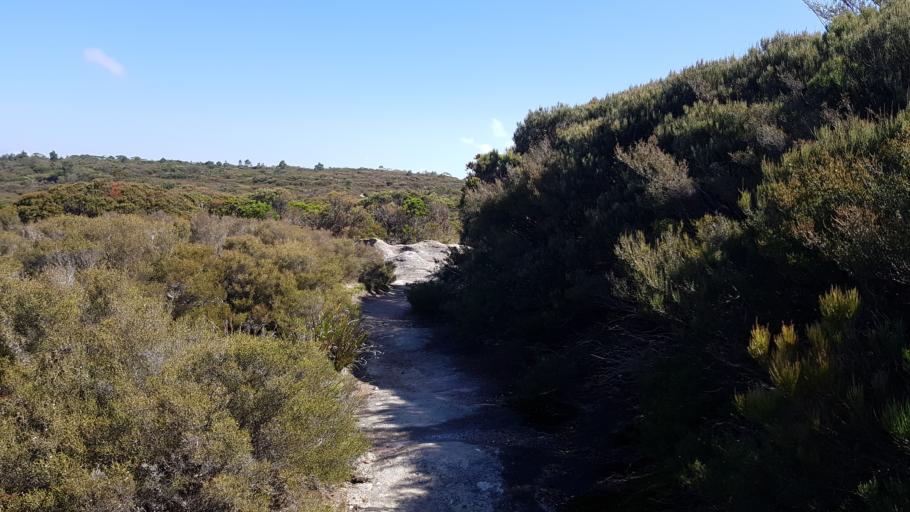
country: AU
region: New South Wales
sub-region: Blue Mountains Municipality
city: Katoomba
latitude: -33.9866
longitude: 150.1176
